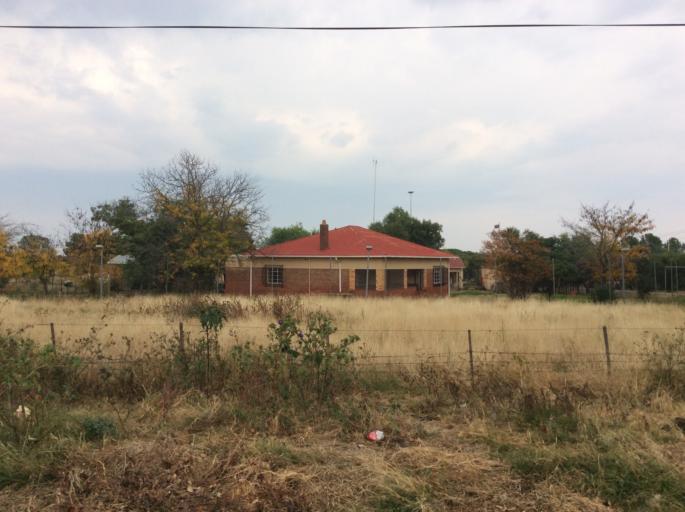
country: LS
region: Mafeteng
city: Mafeteng
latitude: -29.9870
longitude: 27.0172
